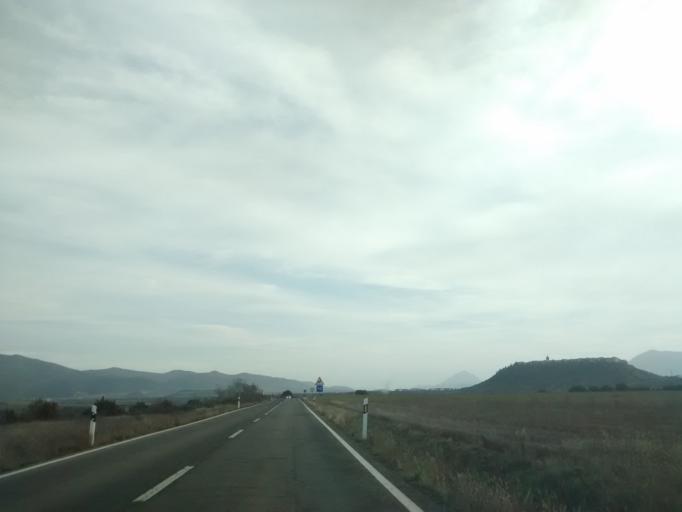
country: ES
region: Aragon
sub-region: Provincia de Zaragoza
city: Mianos
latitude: 42.6108
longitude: -0.8778
